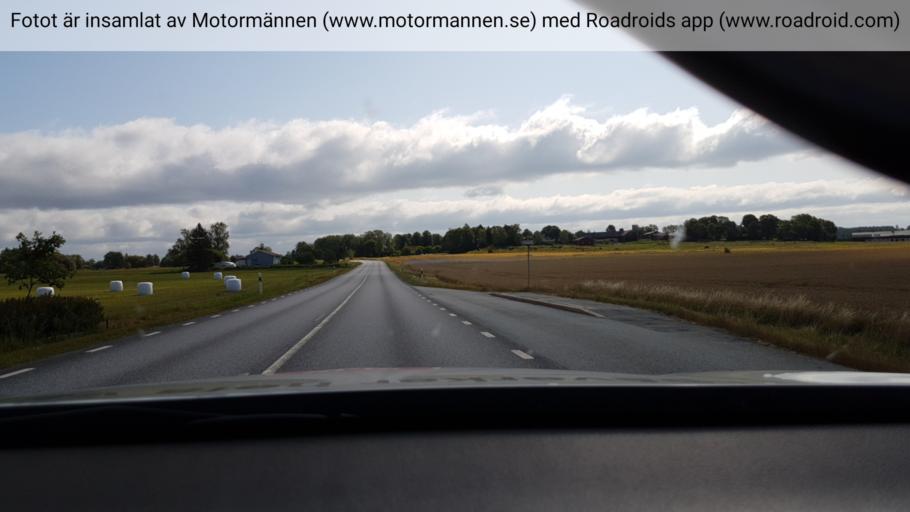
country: SE
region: Stockholm
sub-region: Sigtuna Kommun
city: Marsta
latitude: 59.7516
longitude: 18.0065
